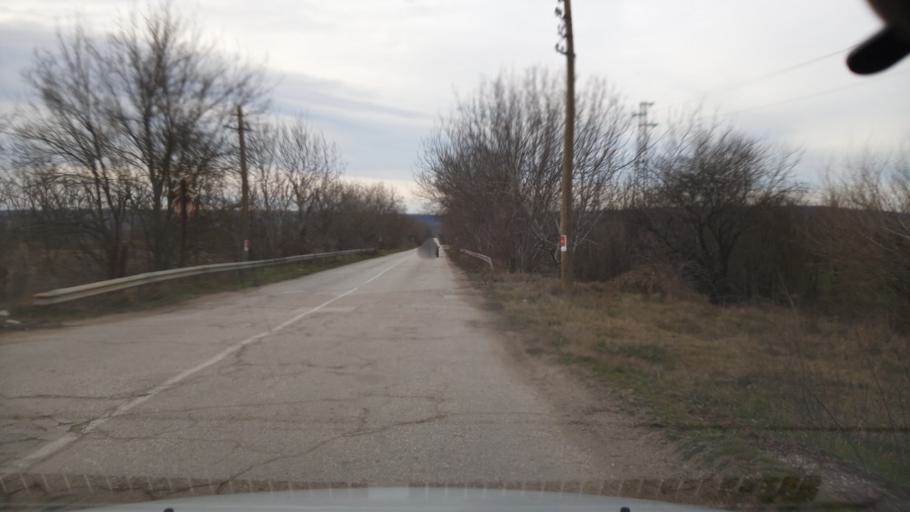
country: BG
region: Pleven
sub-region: Obshtina Belene
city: Belene
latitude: 43.6248
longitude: 25.1210
